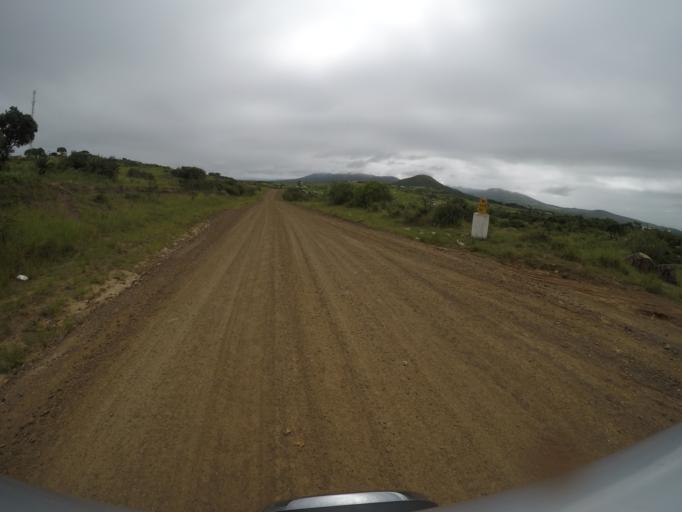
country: ZA
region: KwaZulu-Natal
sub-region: uThungulu District Municipality
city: Empangeni
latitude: -28.6070
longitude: 31.8353
